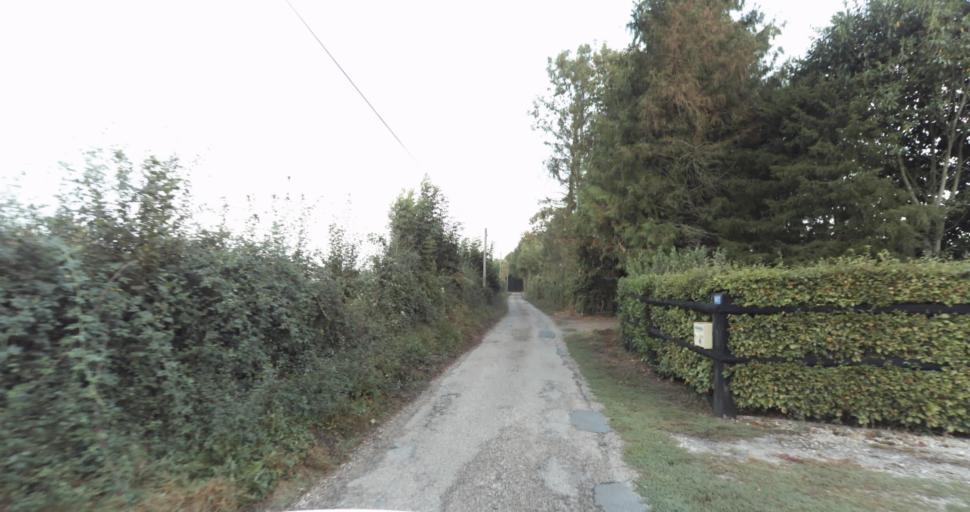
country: FR
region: Lower Normandy
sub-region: Departement de l'Orne
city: Vimoutiers
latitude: 48.9364
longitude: 0.2217
